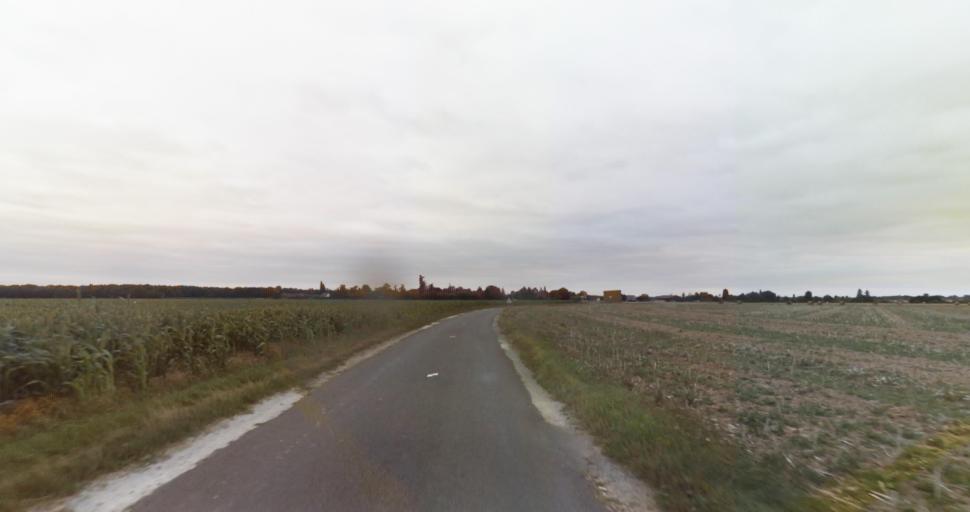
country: FR
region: Haute-Normandie
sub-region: Departement de l'Eure
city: Marcilly-sur-Eure
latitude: 48.8216
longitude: 1.2923
